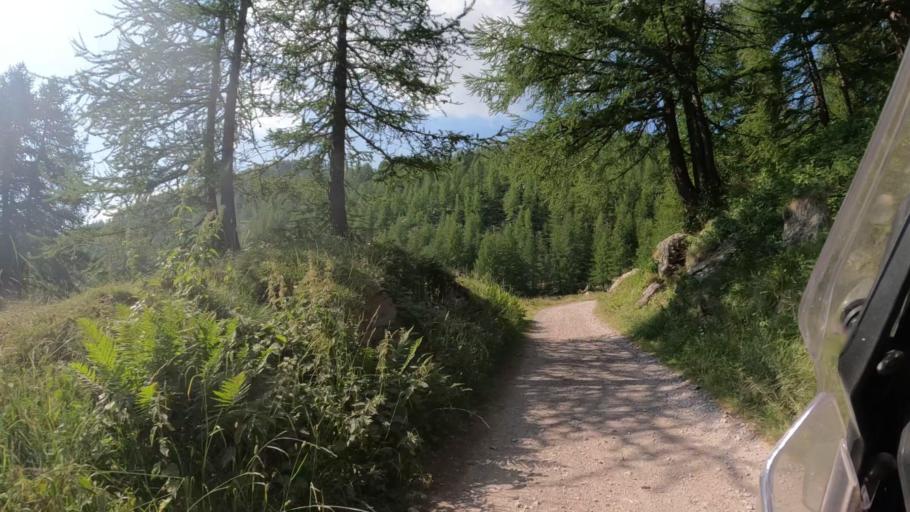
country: IT
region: Piedmont
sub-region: Provincia di Cuneo
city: Briga Alta
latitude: 44.1038
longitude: 7.7096
